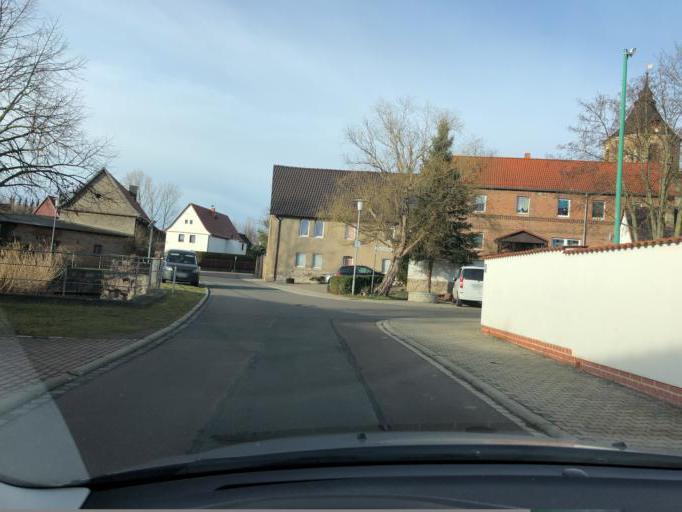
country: DE
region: Saxony-Anhalt
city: Reichardtswerben
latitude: 51.2379
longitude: 11.9505
